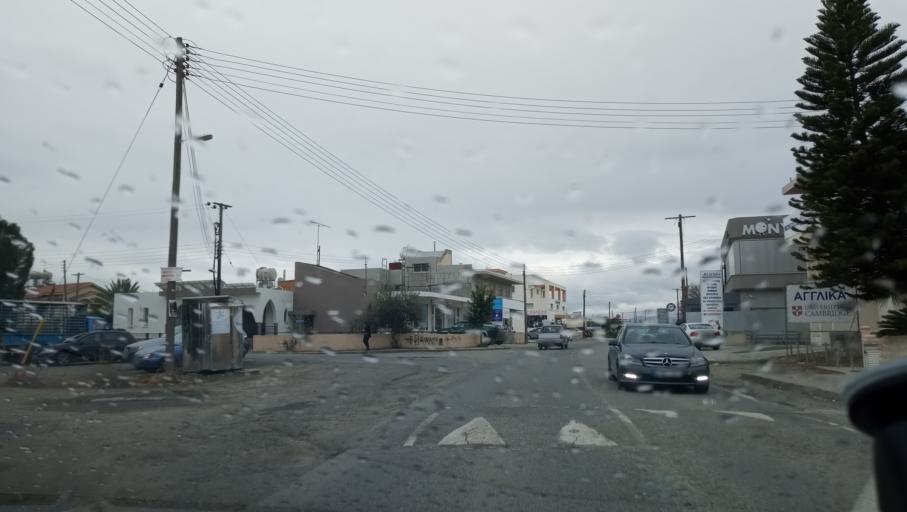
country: CY
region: Lefkosia
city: Kato Deftera
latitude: 35.0832
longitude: 33.2743
